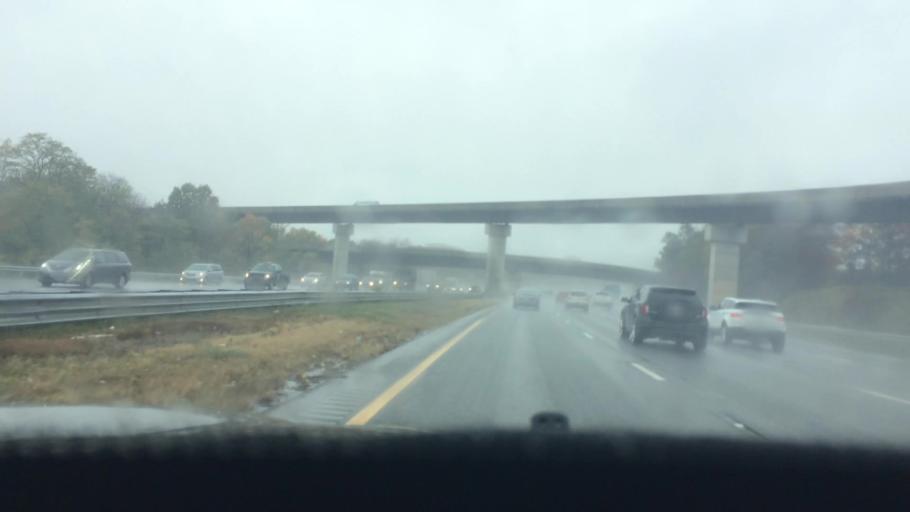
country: US
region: Massachusetts
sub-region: Middlesex County
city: Reading
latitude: 42.5191
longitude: -71.1325
